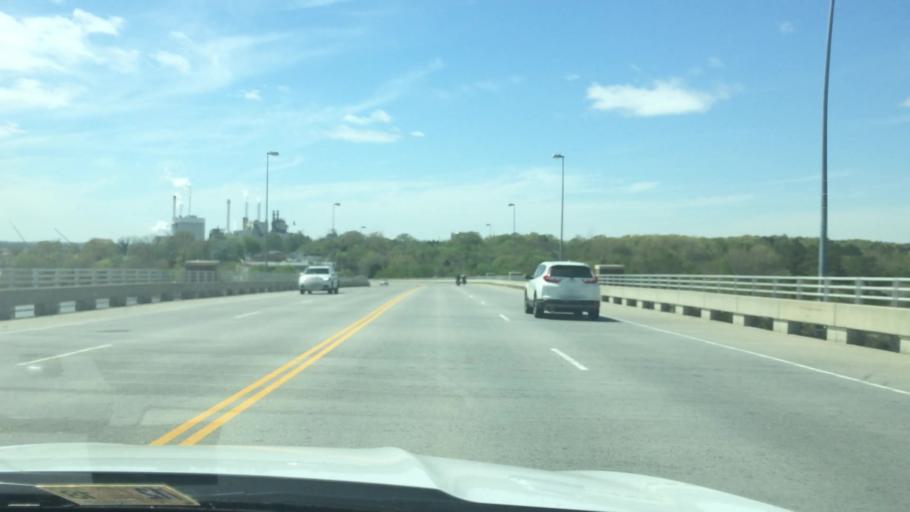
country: US
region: Virginia
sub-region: King William County
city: West Point
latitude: 37.5377
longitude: -76.7899
